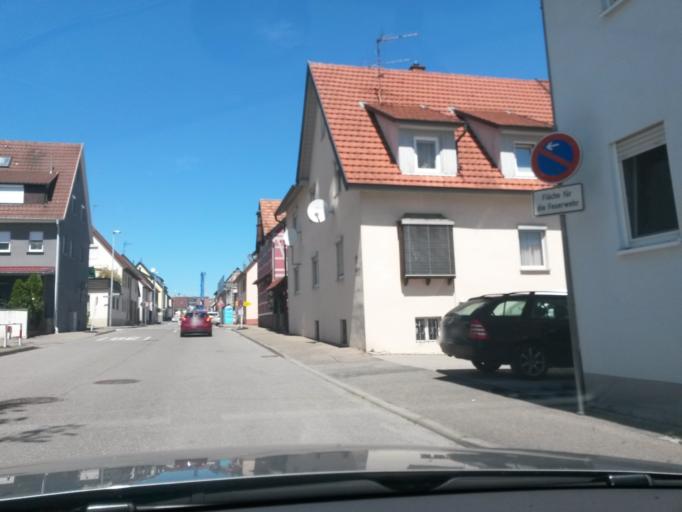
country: DE
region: Baden-Wuerttemberg
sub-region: Regierungsbezirk Stuttgart
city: Weil der Stadt
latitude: 48.7676
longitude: 8.8505
